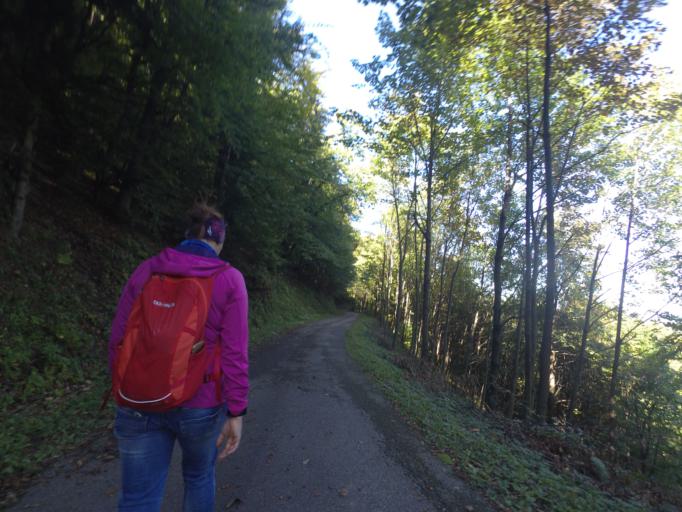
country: AT
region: Styria
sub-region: Politischer Bezirk Leibnitz
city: Kitzeck im Sausal
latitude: 46.7828
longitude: 15.4336
